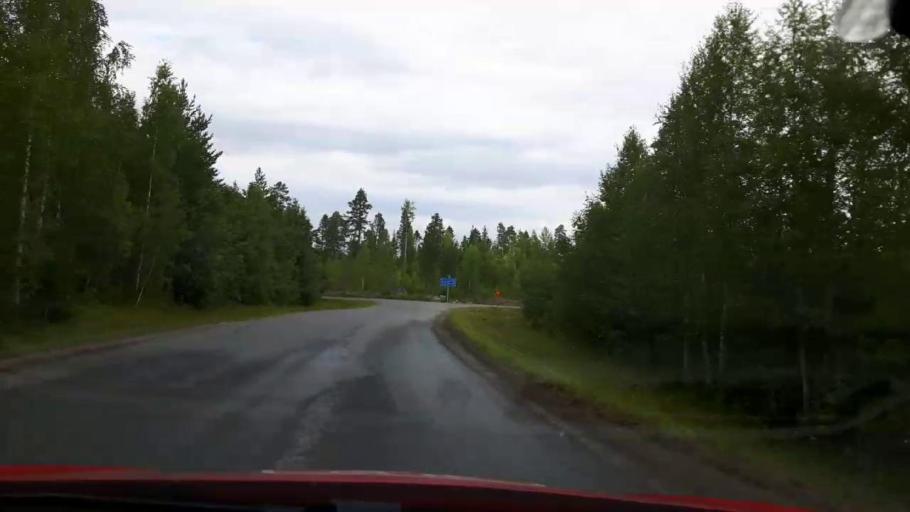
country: SE
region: Jaemtland
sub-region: Stroemsunds Kommun
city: Stroemsund
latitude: 63.8163
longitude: 15.6248
